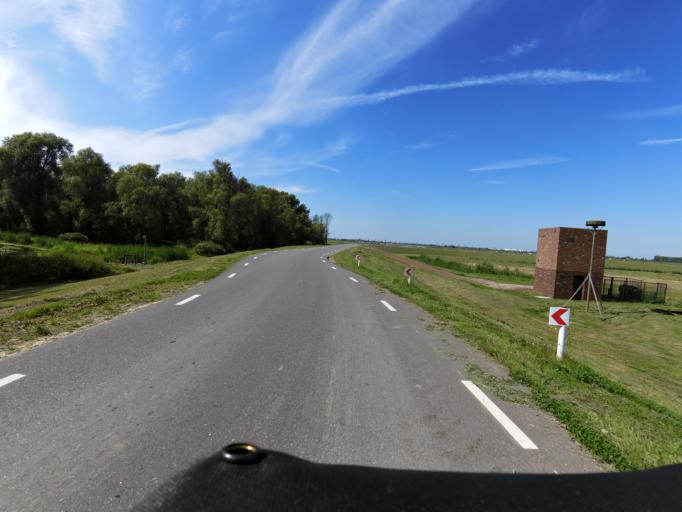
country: NL
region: North Brabant
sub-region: Gemeente Werkendam
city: Werkendam
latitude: 51.7827
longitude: 4.8631
